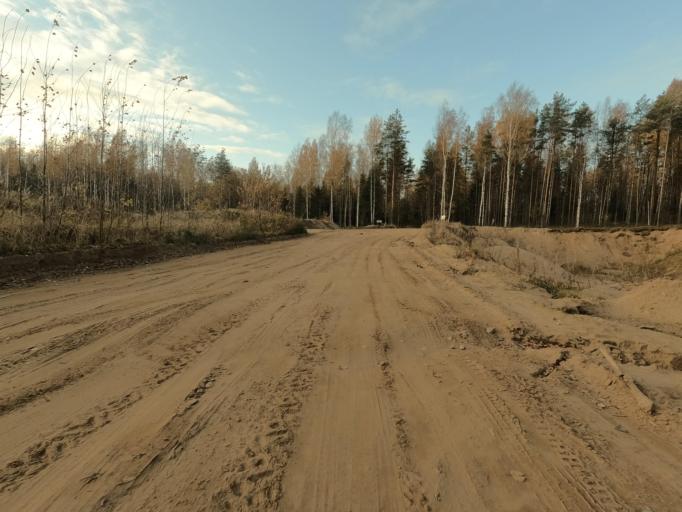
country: RU
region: Leningrad
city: Priladozhskiy
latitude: 59.7389
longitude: 31.3168
